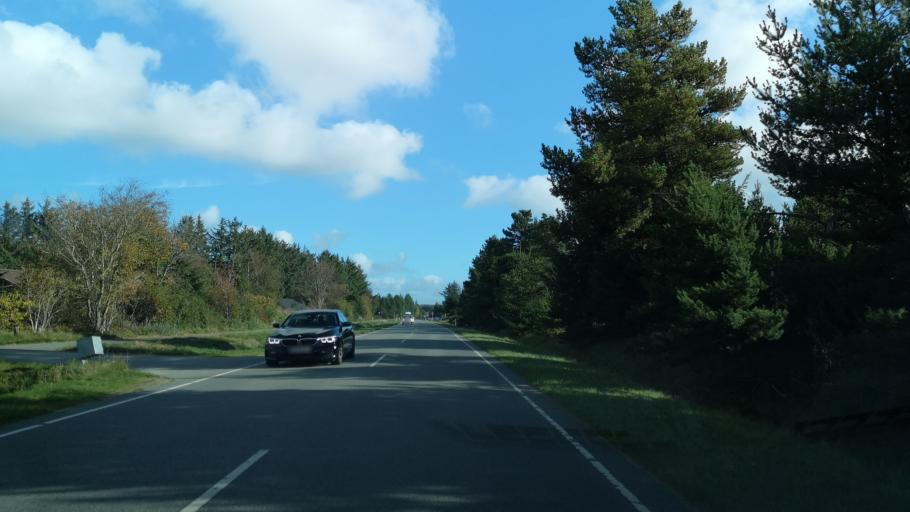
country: DK
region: South Denmark
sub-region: Varde Kommune
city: Oksbol
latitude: 55.7316
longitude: 8.2095
